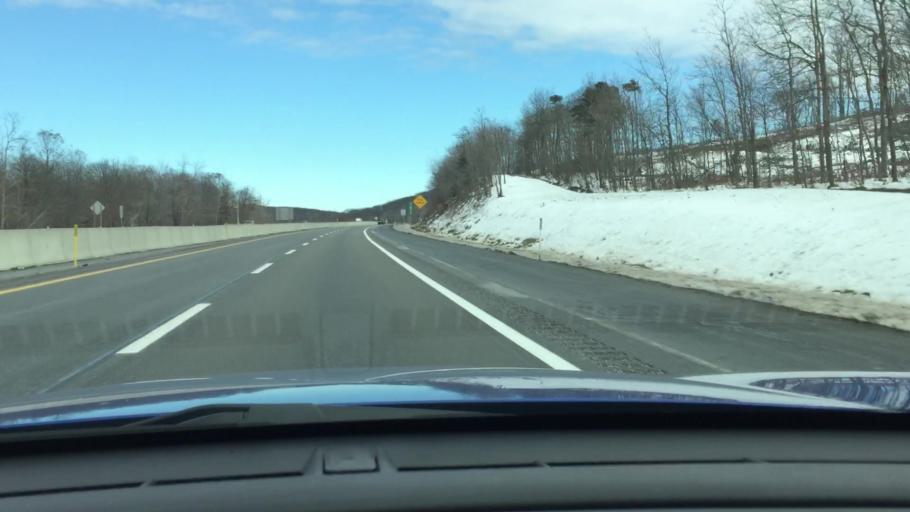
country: US
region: Pennsylvania
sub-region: Fulton County
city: McConnellsburg
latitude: 40.0293
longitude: -78.1692
